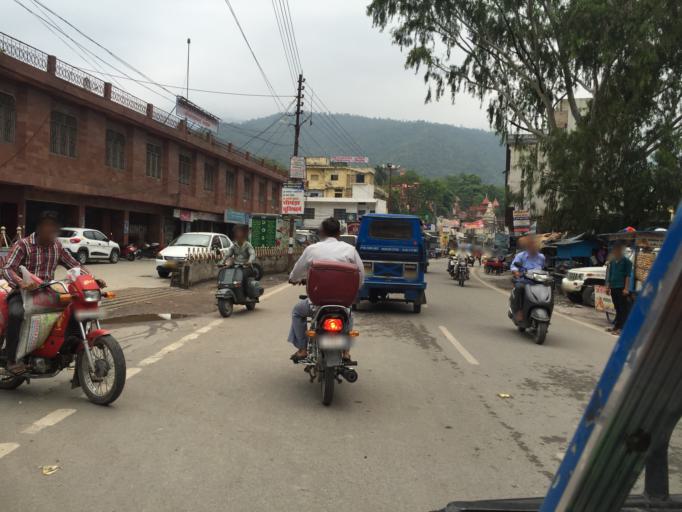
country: IN
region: Uttarakhand
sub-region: Dehradun
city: Rishikesh
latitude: 30.1158
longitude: 78.3032
